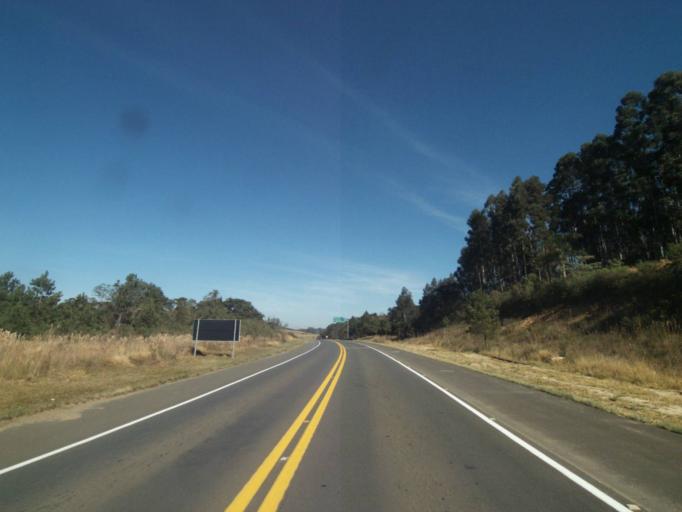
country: BR
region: Parana
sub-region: Tibagi
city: Tibagi
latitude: -24.8104
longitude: -50.4820
